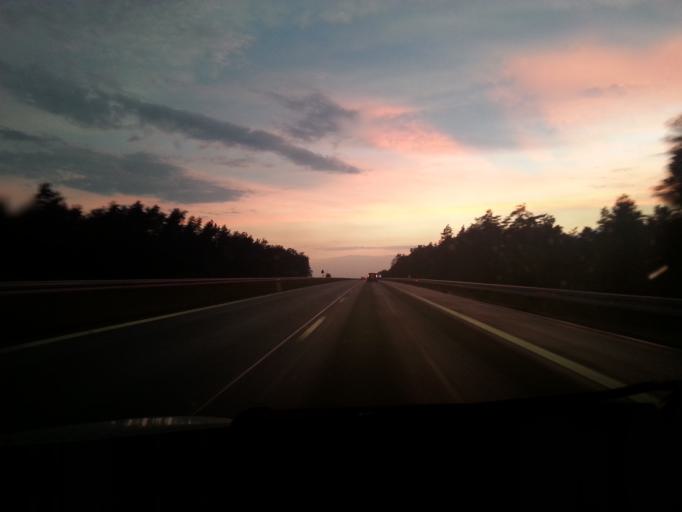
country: PL
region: Lodz Voivodeship
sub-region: Powiat zdunskowolski
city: Zdunska Wola
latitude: 51.5726
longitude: 18.9560
